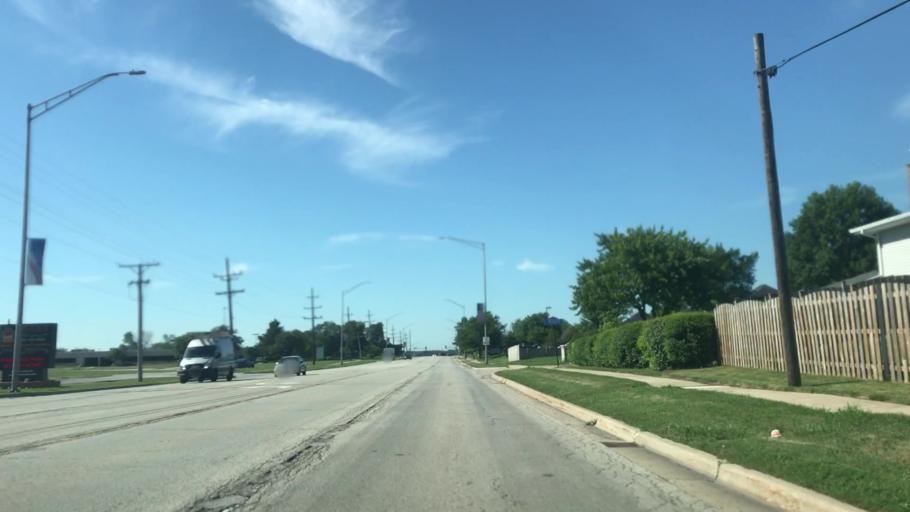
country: US
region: Illinois
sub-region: DuPage County
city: Darien
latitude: 41.7419
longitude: -87.9736
